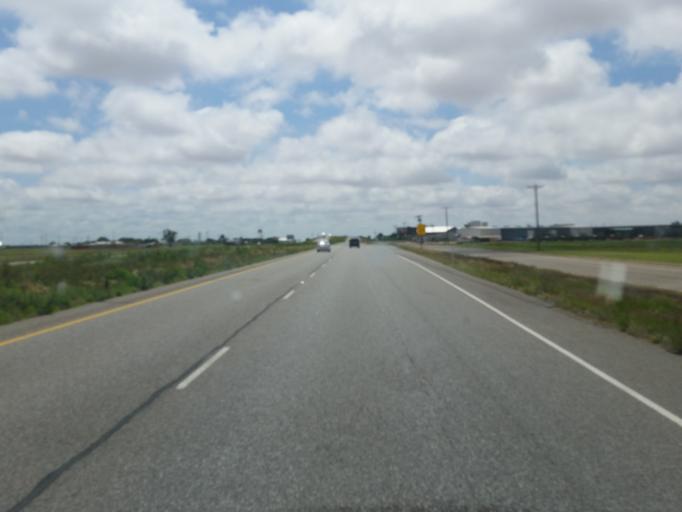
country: US
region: Texas
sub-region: Lubbock County
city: Slaton
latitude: 33.4238
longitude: -101.6497
